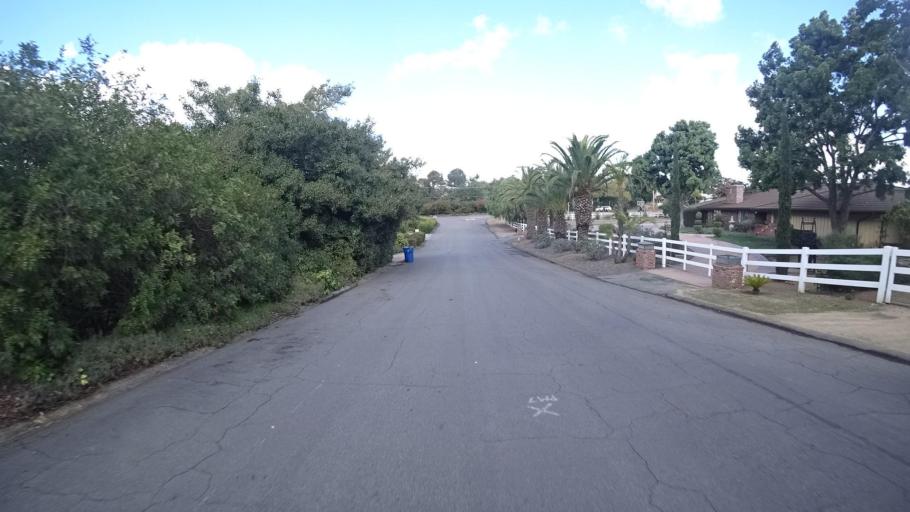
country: US
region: California
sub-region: San Diego County
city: Casa de Oro-Mount Helix
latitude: 32.7651
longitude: -116.9677
